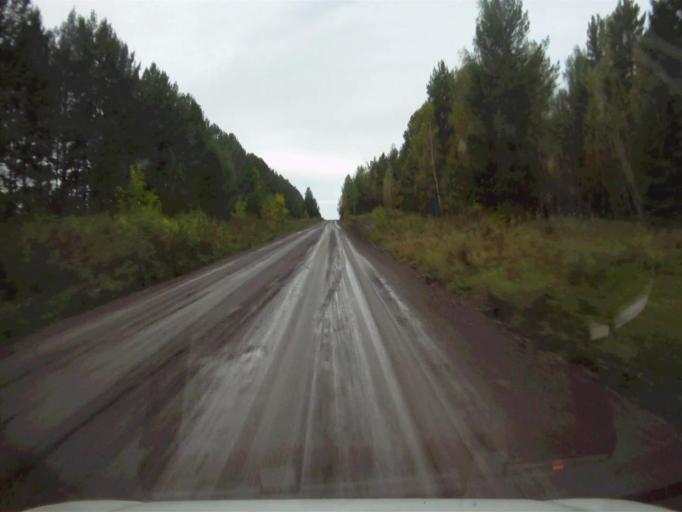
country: RU
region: Chelyabinsk
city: Nyazepetrovsk
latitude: 56.1416
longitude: 59.2915
